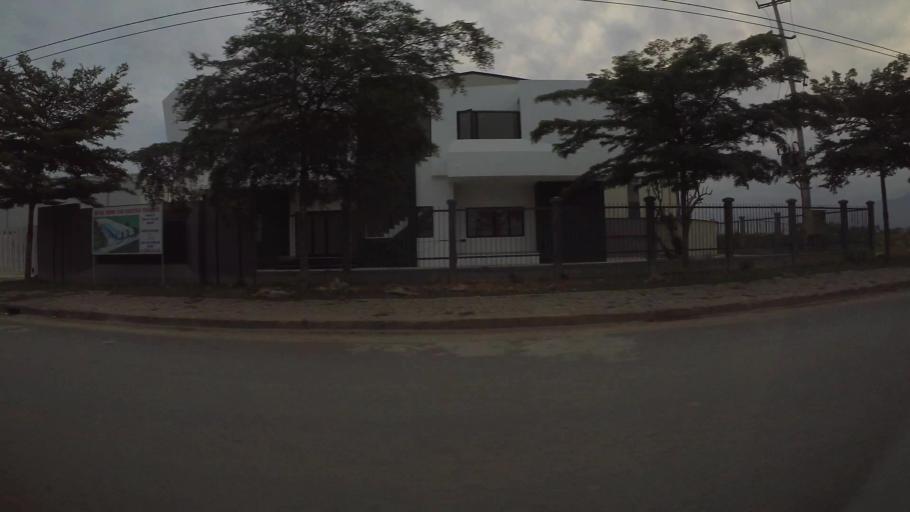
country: VN
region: Da Nang
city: Lien Chieu
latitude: 16.0889
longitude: 108.1101
